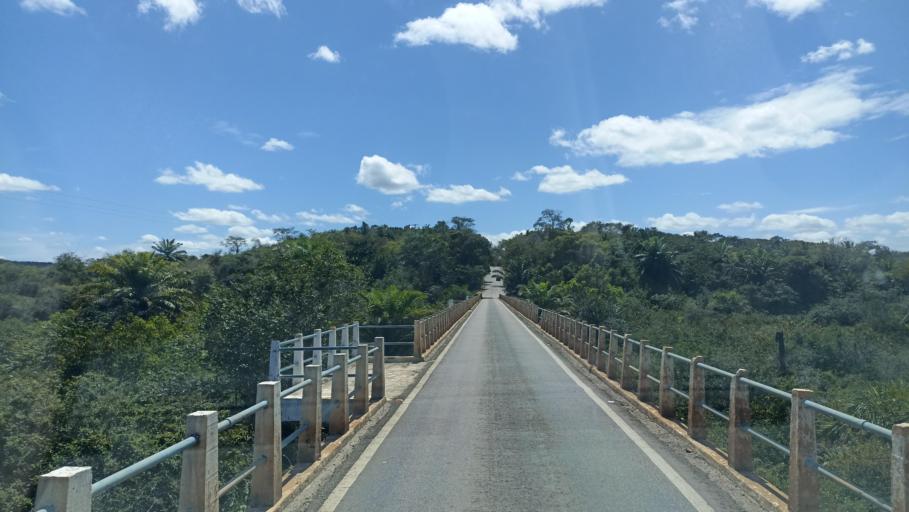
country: BR
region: Bahia
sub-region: Andarai
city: Vera Cruz
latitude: -12.7563
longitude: -41.3289
